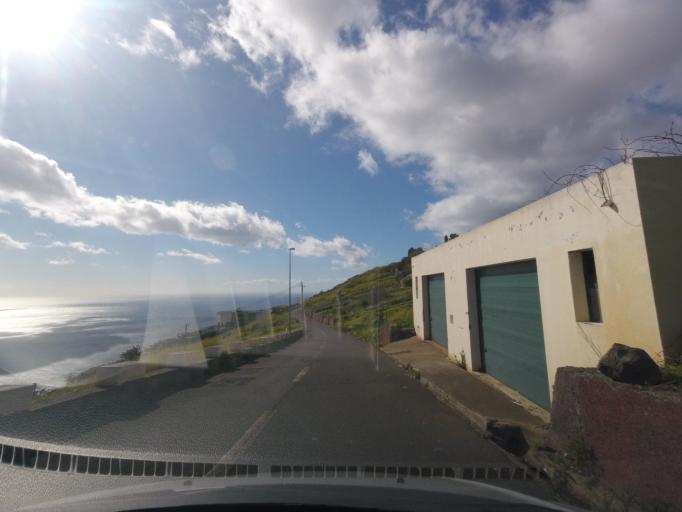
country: PT
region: Madeira
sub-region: Ribeira Brava
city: Campanario
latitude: 32.6630
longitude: -17.0247
